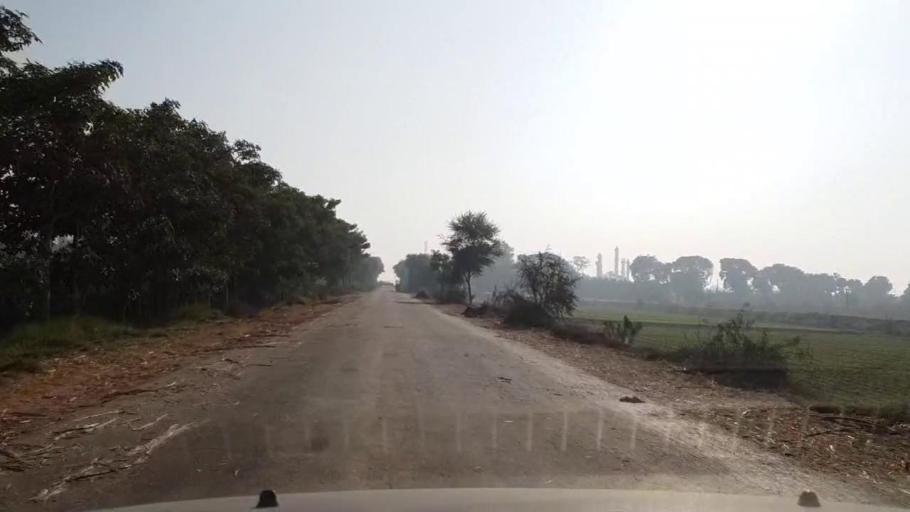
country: PK
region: Sindh
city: Matiari
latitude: 25.5813
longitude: 68.4950
